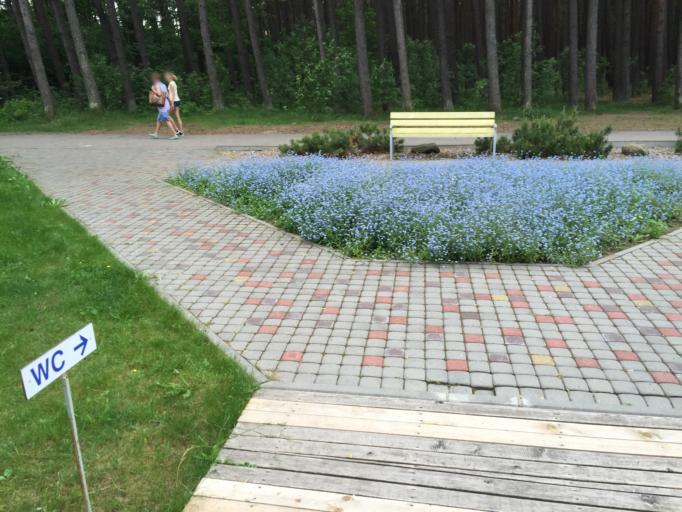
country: LT
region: Klaipedos apskritis
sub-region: Klaipeda
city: Palanga
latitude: 55.9291
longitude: 21.0629
